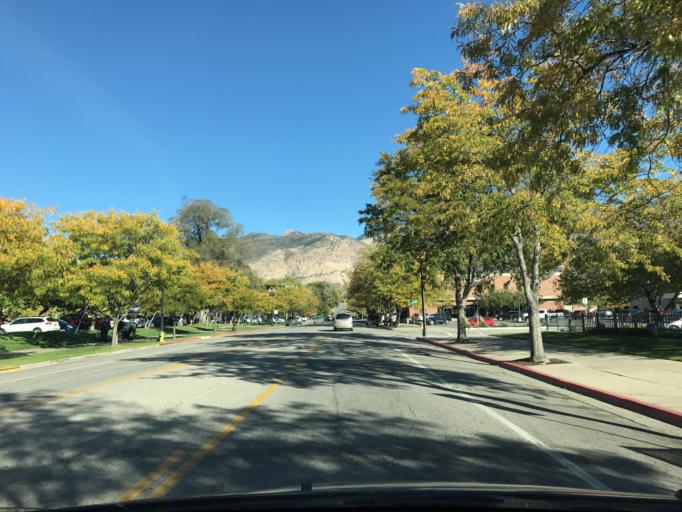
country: US
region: Utah
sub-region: Weber County
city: Ogden
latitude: 41.2186
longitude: -111.9727
